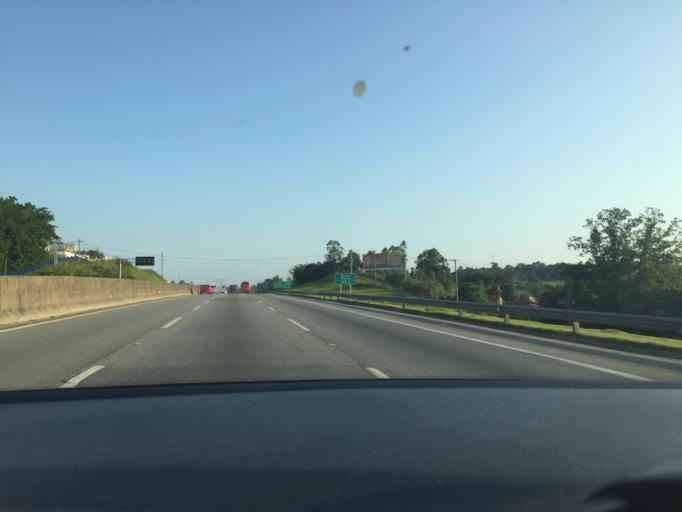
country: BR
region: Sao Paulo
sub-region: Louveira
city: Louveira
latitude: -23.1069
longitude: -46.9620
